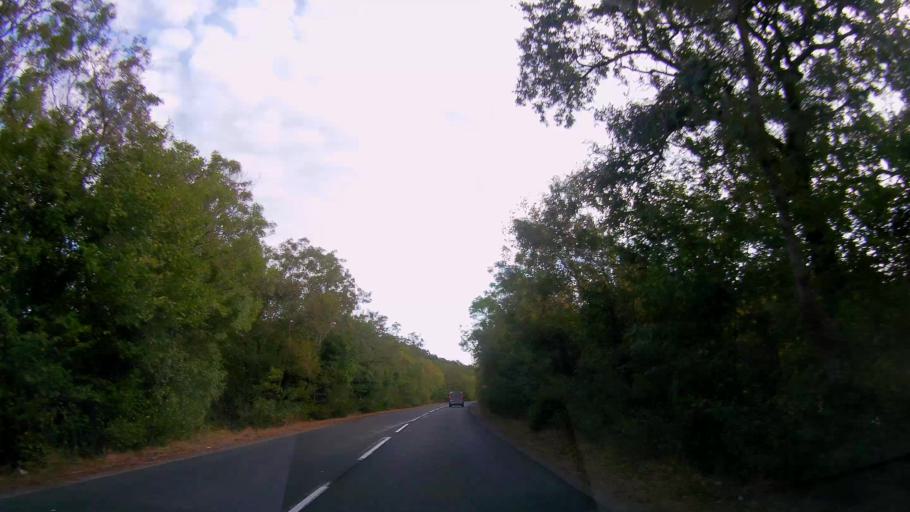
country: BG
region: Burgas
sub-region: Obshtina Primorsko
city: Primorsko
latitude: 42.3140
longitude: 27.7276
